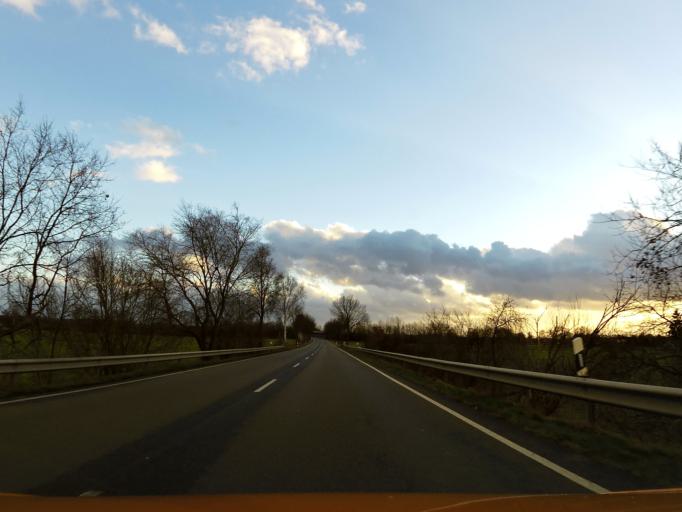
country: DE
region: Lower Saxony
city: Broeckel
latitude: 52.5177
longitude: 10.2232
